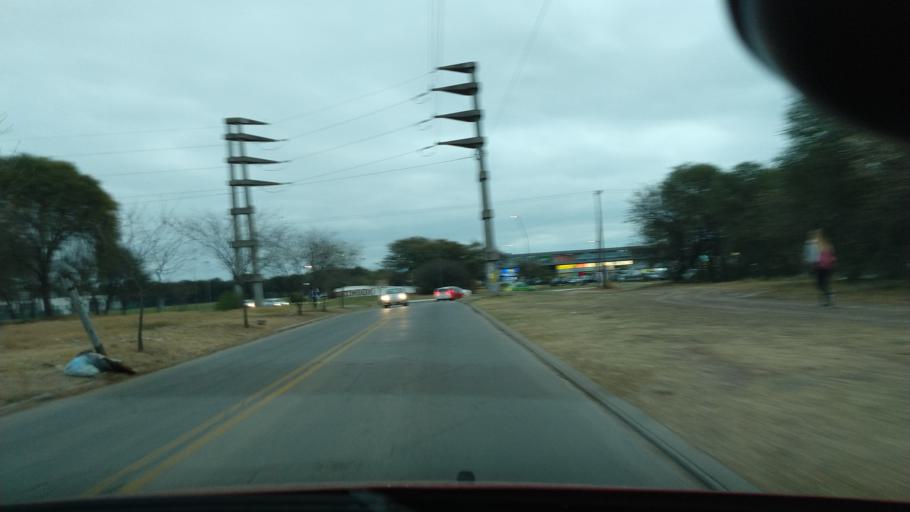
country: AR
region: Cordoba
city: La Calera
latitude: -31.3784
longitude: -64.2756
